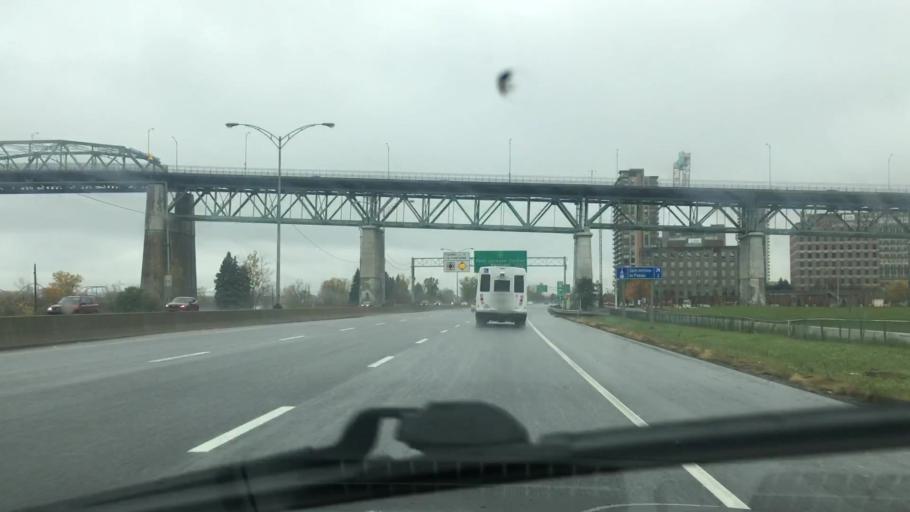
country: CA
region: Quebec
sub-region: Monteregie
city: Longueuil
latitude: 45.5194
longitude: -73.5235
